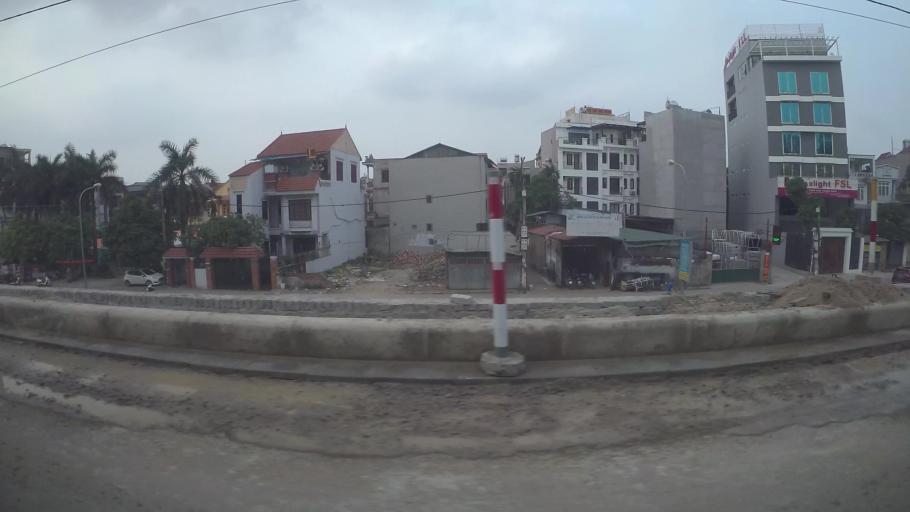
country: VN
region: Ha Noi
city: Trau Quy
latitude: 21.0211
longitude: 105.8991
